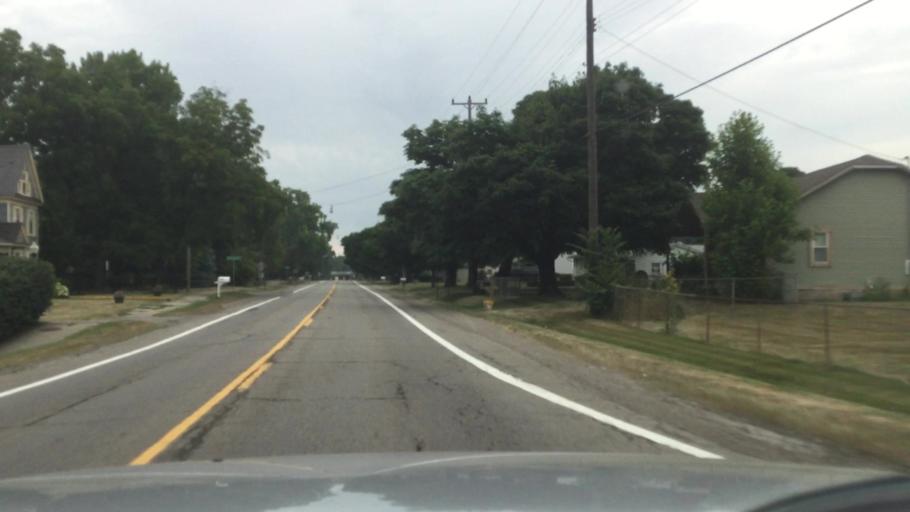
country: US
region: Michigan
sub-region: Oakland County
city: Waterford
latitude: 42.6833
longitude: -83.4208
